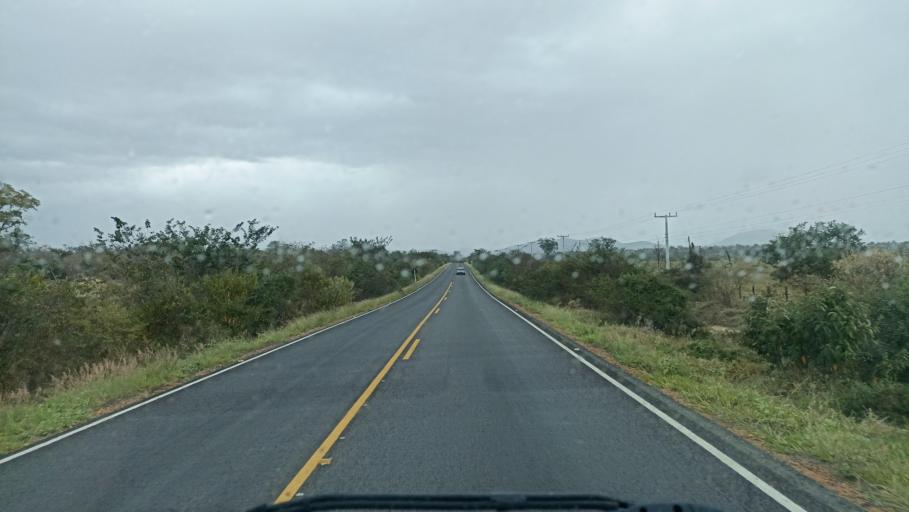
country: BR
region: Bahia
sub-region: Maracas
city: Maracas
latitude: -13.0416
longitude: -40.7035
